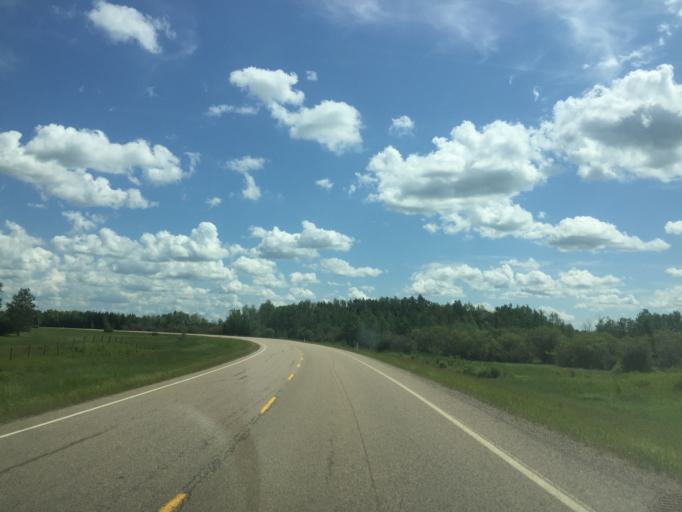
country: CA
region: Alberta
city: Athabasca
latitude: 54.3287
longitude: -113.3233
